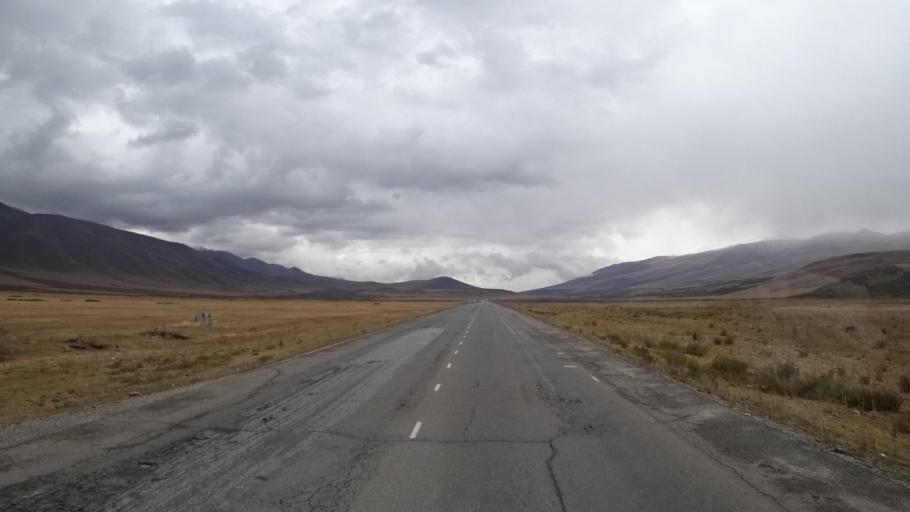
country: KG
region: Jalal-Abad
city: Uch-Terek
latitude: 42.1899
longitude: 73.4942
